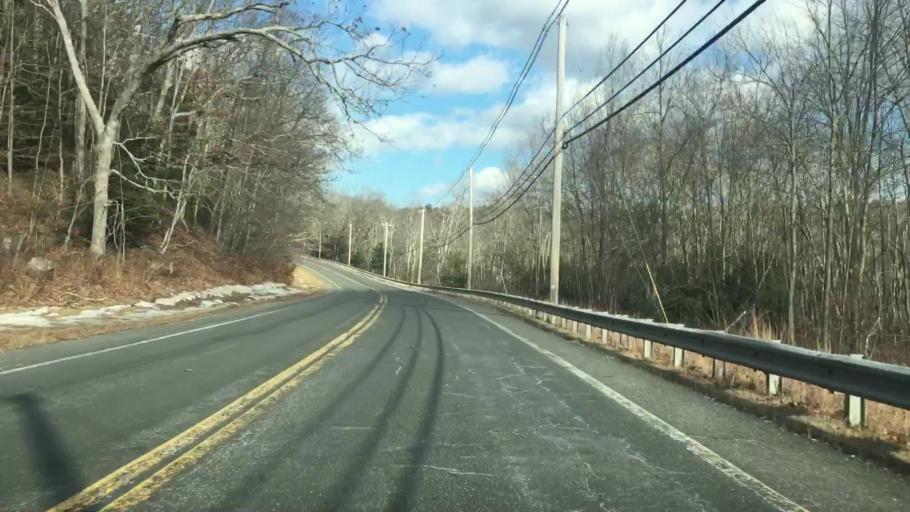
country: US
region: Massachusetts
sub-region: Hampden County
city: Wales
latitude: 42.0810
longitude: -72.2013
